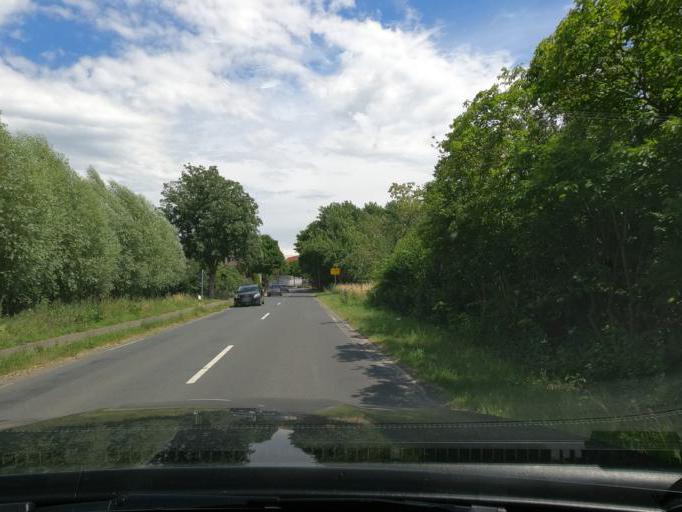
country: DE
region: Lower Saxony
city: Lengede
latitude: 52.1910
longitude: 10.3206
